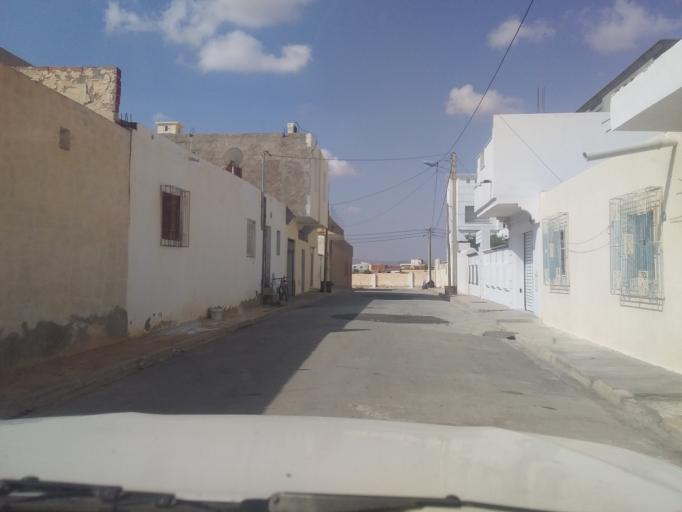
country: TN
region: Qabis
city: Matmata
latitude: 33.6204
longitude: 10.2802
